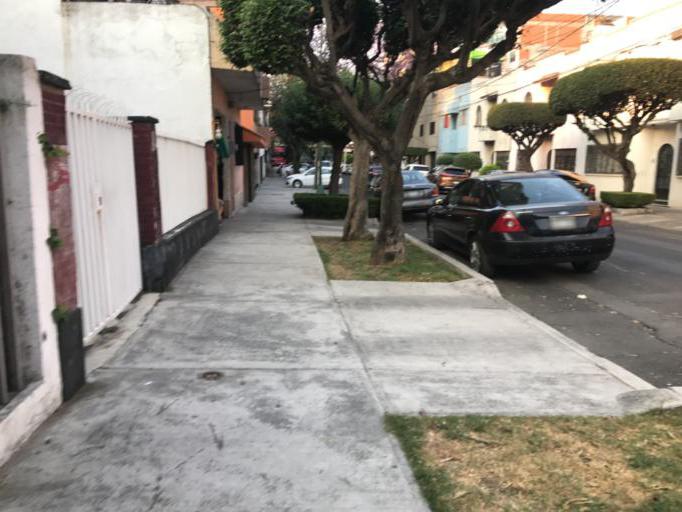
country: MX
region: Mexico City
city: Benito Juarez
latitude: 19.3946
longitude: -99.1520
